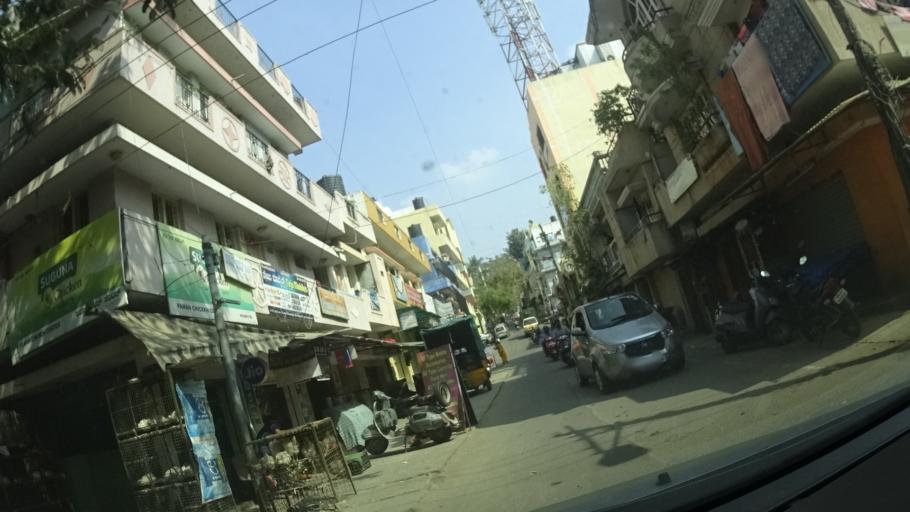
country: IN
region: Karnataka
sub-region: Bangalore Urban
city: Bangalore
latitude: 12.9489
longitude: 77.5554
